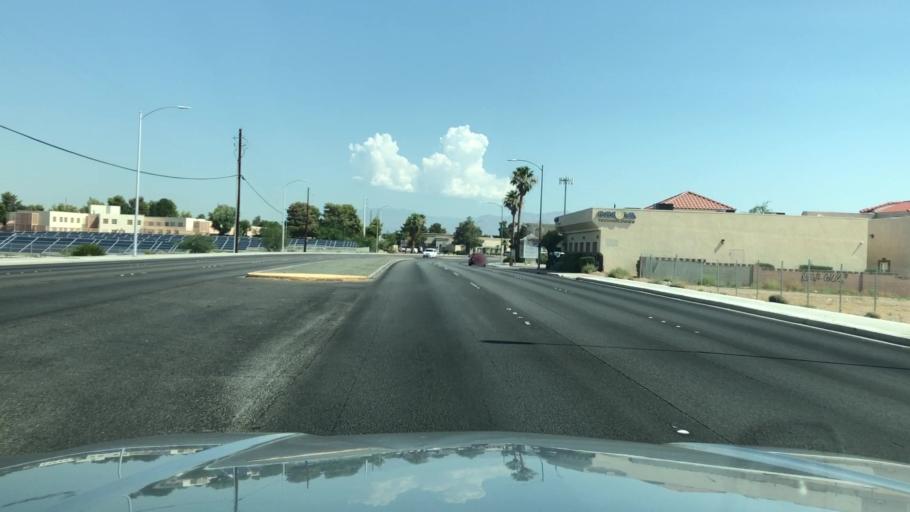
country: US
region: Nevada
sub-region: Clark County
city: Spring Valley
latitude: 36.1544
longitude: -115.2257
